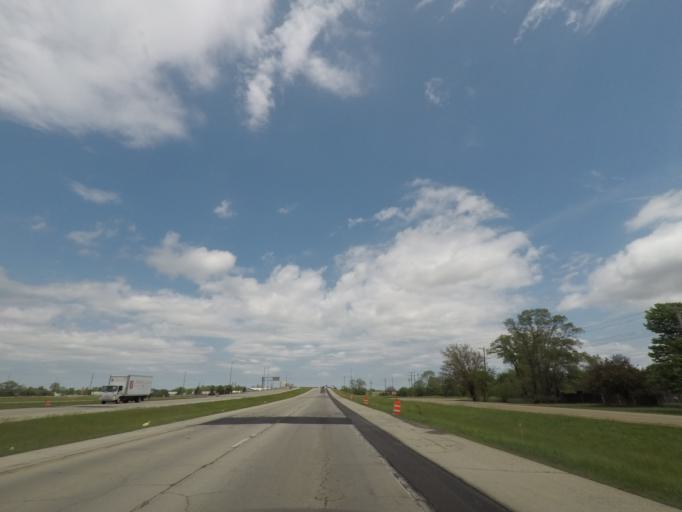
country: US
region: Illinois
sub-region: Winnebago County
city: Roscoe
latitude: 42.4533
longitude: -89.0192
